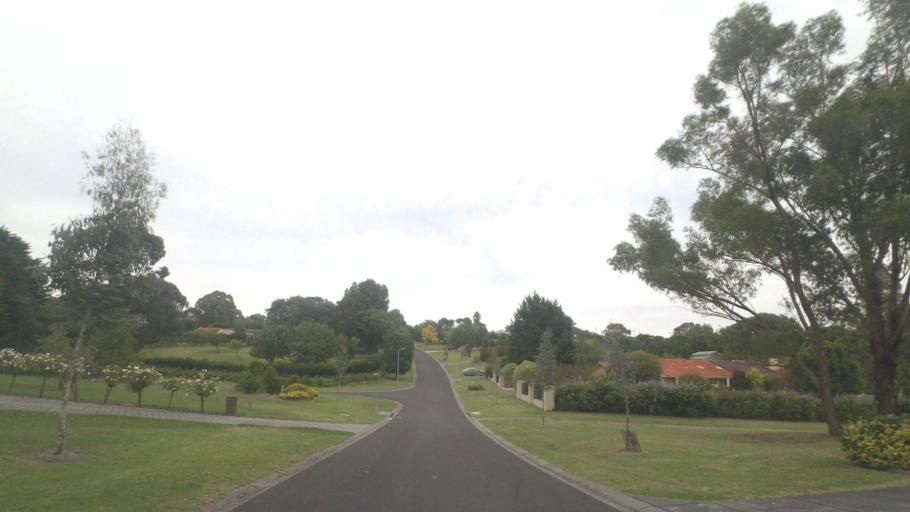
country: AU
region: Victoria
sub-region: Nillumbik
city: North Warrandyte
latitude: -37.7467
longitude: 145.1877
